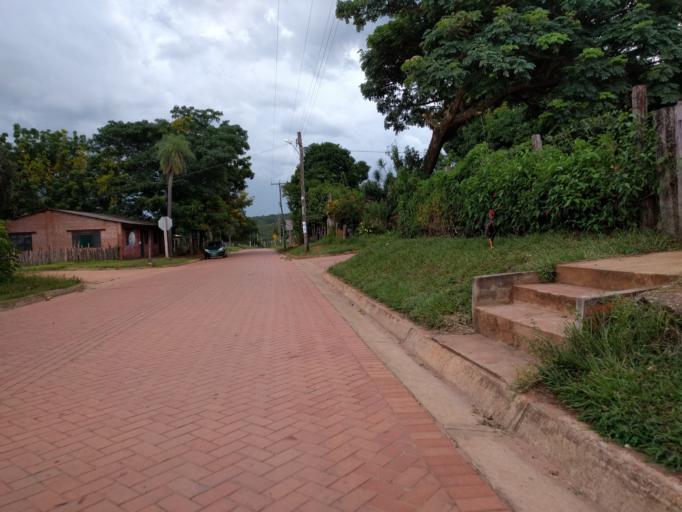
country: BO
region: Santa Cruz
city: Robore
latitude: -18.3412
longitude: -59.6005
